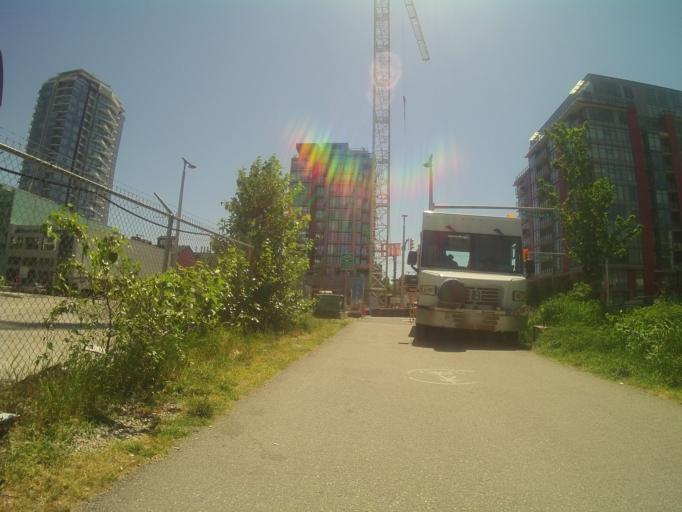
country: CA
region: British Columbia
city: Vancouver
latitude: 49.2706
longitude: -123.1044
